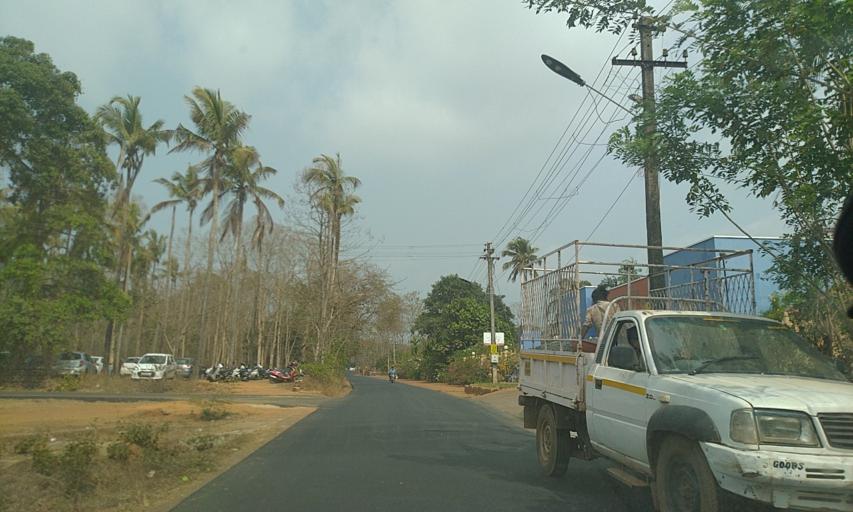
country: IN
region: Goa
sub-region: South Goa
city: Raia
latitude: 15.3078
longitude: 73.9637
